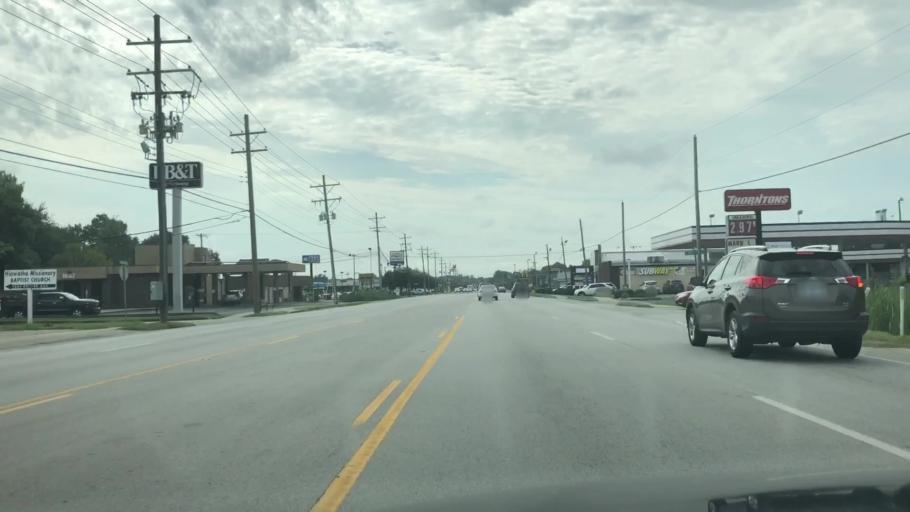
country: US
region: Kentucky
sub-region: Jefferson County
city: Audubon Park
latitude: 38.1715
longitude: -85.7096
